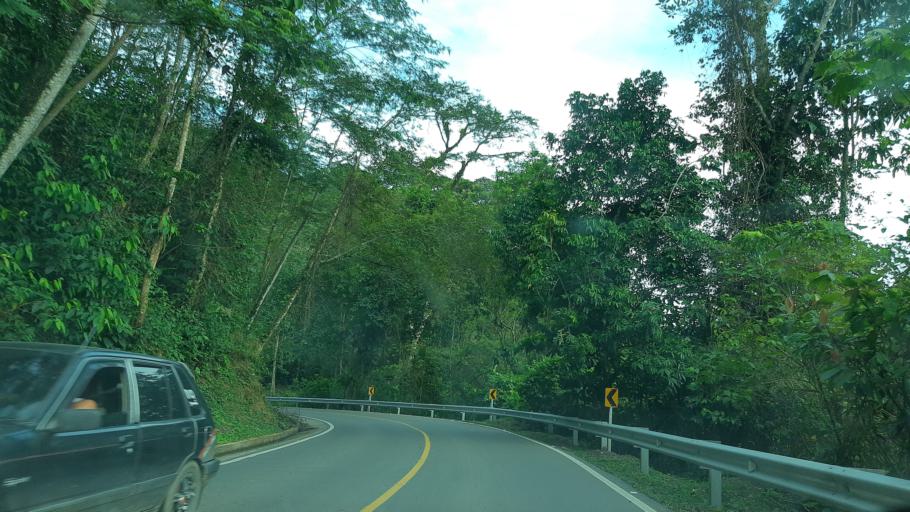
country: CO
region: Boyaca
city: San Luis de Gaceno
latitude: 4.8402
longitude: -73.2154
